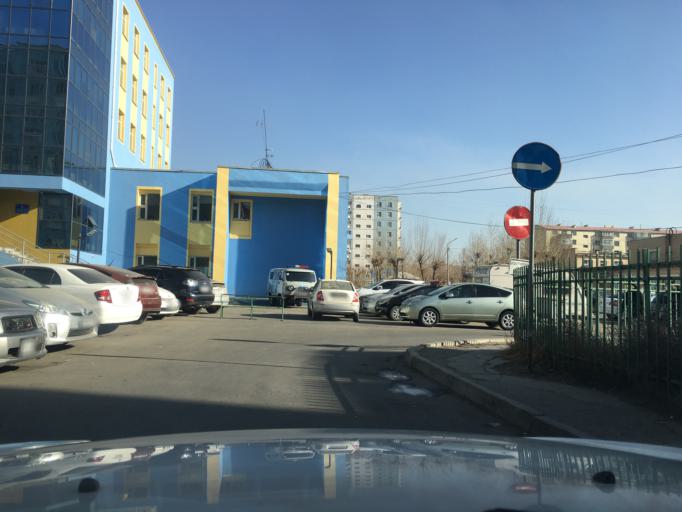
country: MN
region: Ulaanbaatar
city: Ulaanbaatar
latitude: 47.9159
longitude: 106.8463
